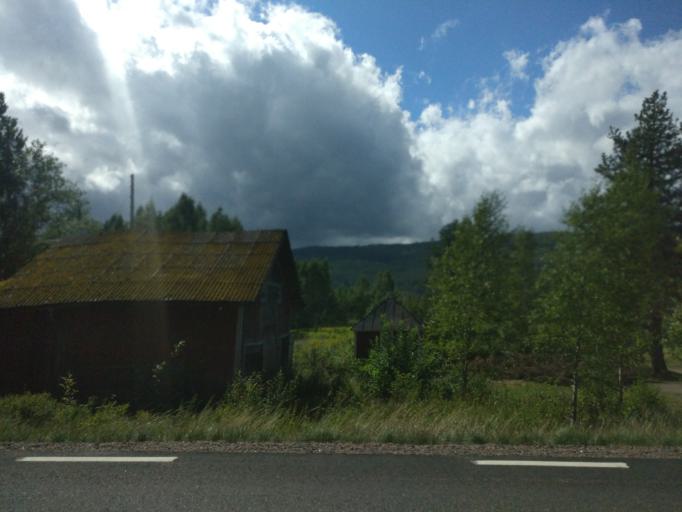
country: SE
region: Vaermland
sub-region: Hagfors Kommun
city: Ekshaerad
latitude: 60.3522
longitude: 13.3346
